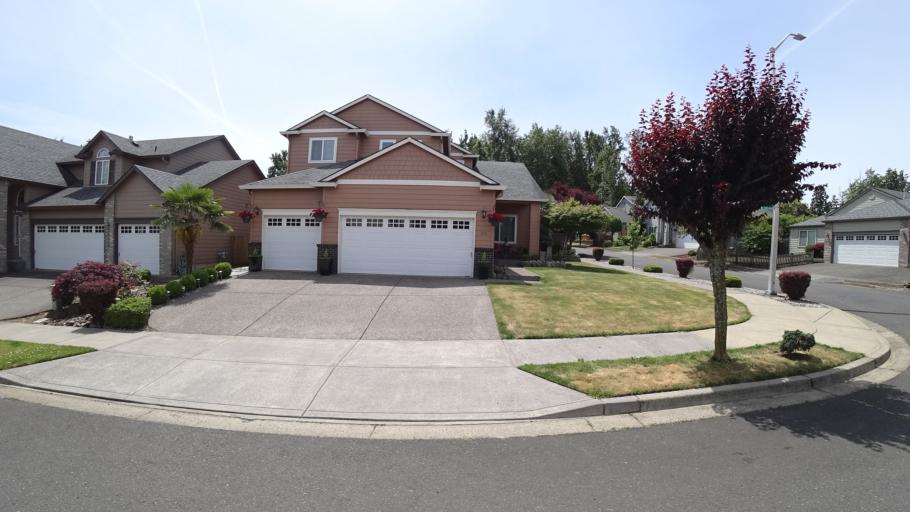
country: US
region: Oregon
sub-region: Multnomah County
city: Fairview
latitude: 45.5479
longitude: -122.4943
